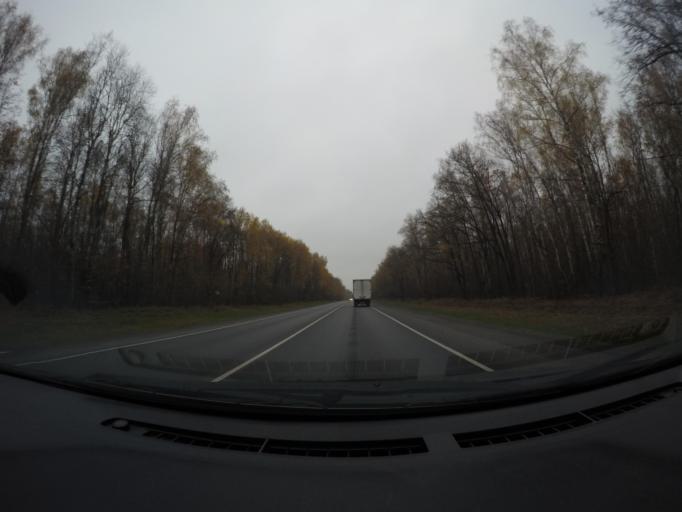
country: RU
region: Moskovskaya
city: Bronnitsy
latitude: 55.3728
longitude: 38.1296
